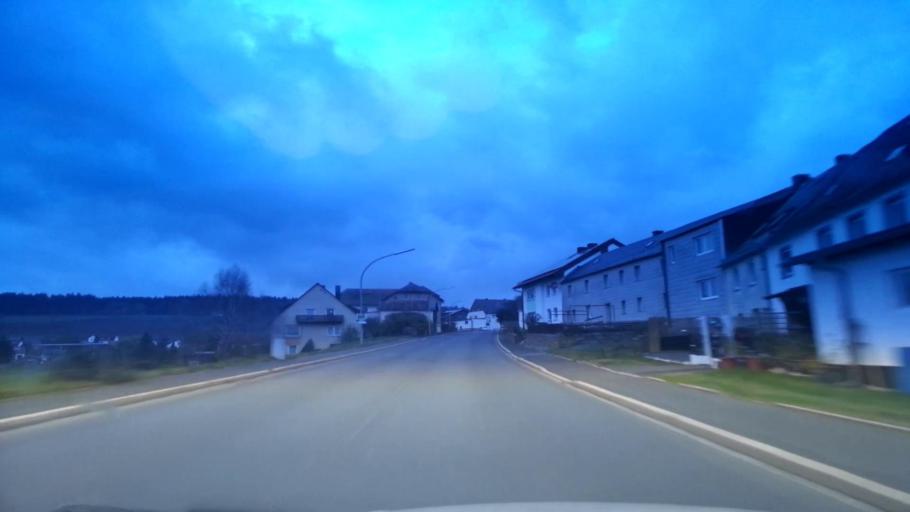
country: DE
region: Bavaria
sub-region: Upper Palatinate
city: Fuchsmuhl
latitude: 49.9202
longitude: 12.1478
